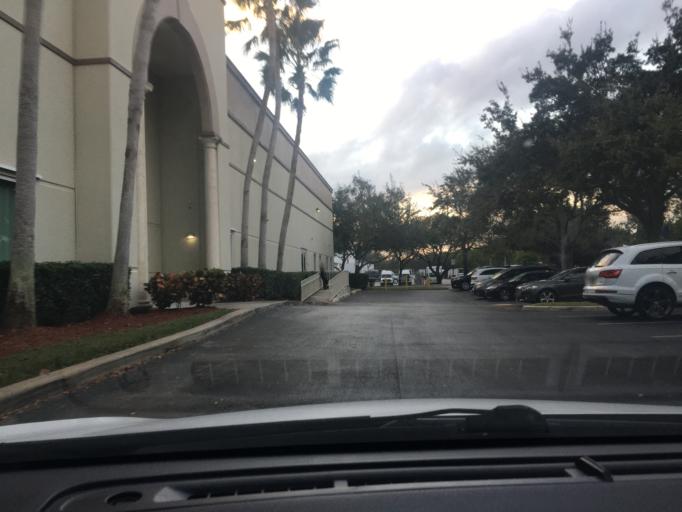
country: US
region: Florida
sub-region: Broward County
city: Broadview Park
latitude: 26.0712
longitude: -80.1798
